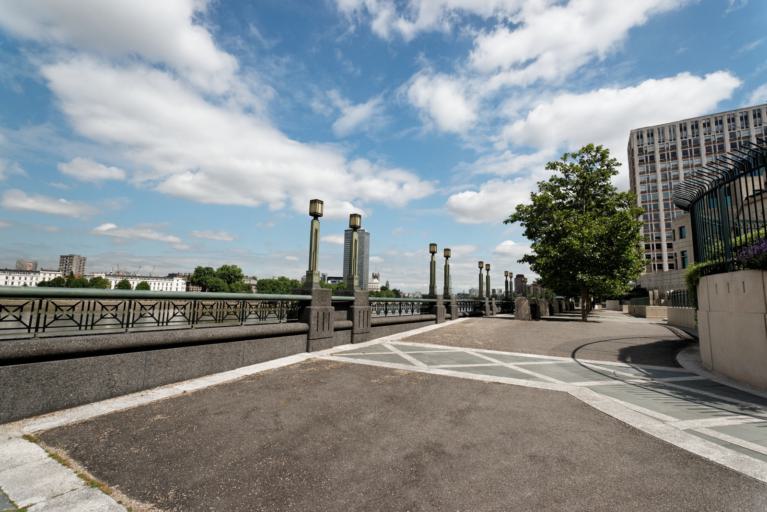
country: GB
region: England
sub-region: Greater London
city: City of Westminster
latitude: 51.4873
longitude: -0.1259
